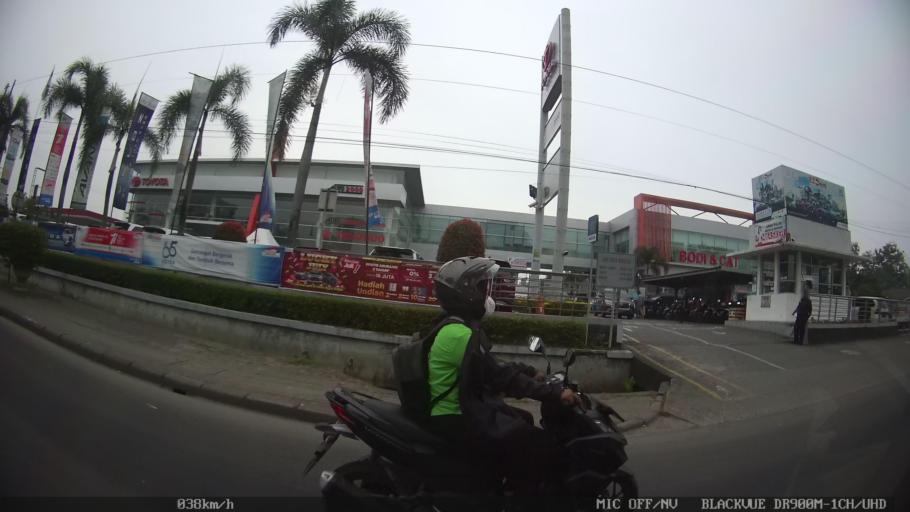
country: ID
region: North Sumatra
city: Deli Tua
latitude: 3.5330
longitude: 98.7239
